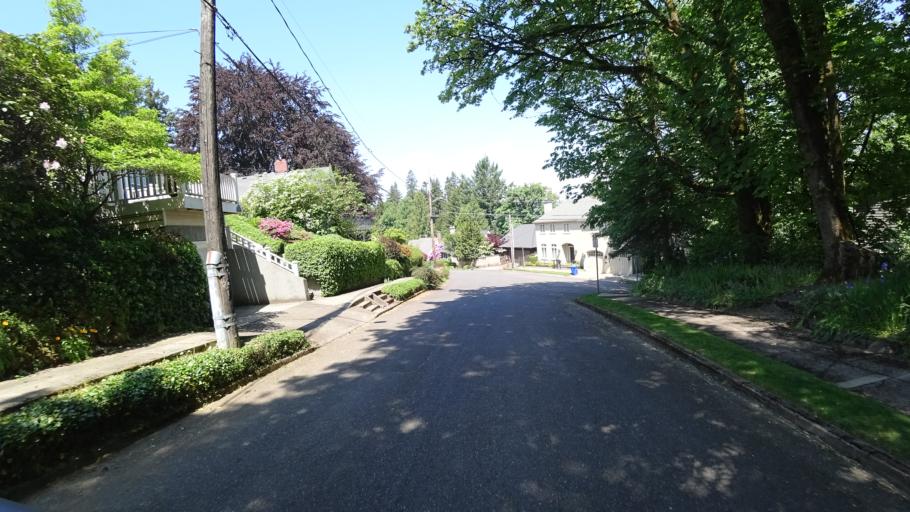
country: US
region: Oregon
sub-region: Multnomah County
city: Portland
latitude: 45.4952
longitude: -122.7010
